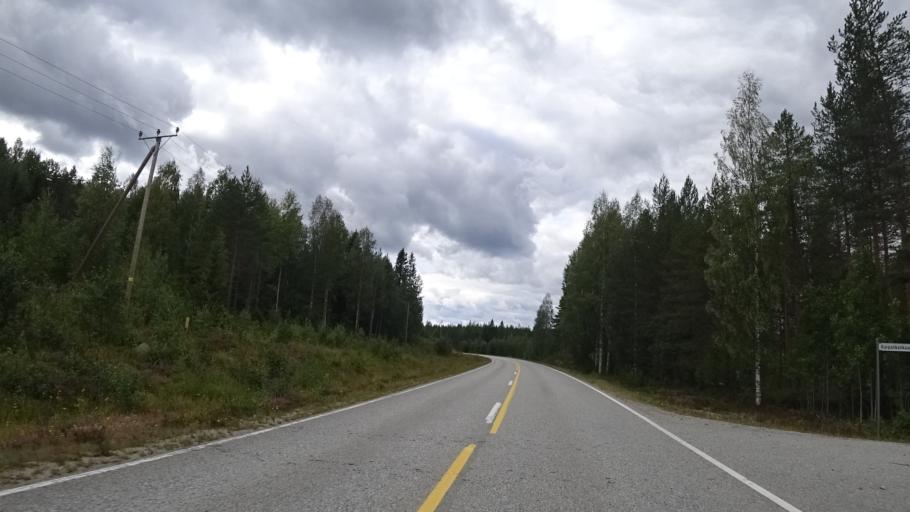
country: FI
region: North Karelia
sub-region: Joensuu
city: Ilomantsi
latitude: 62.6247
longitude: 31.2462
